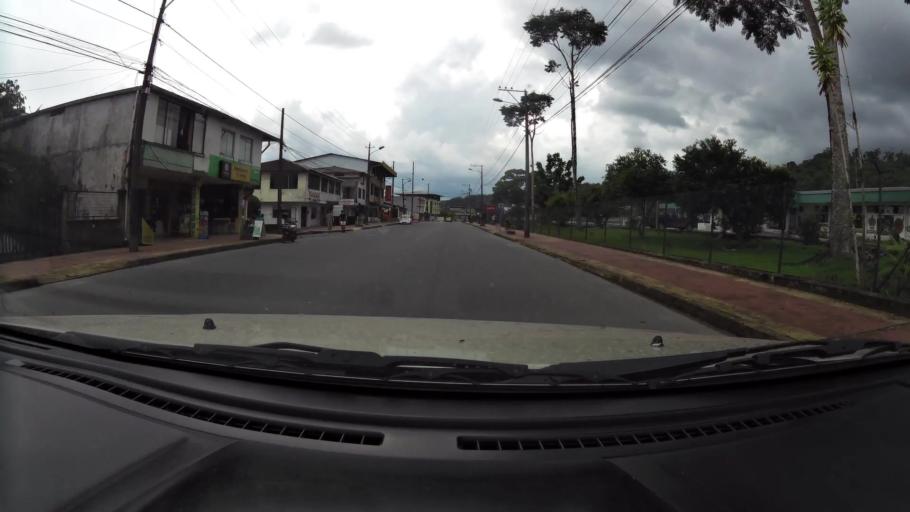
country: EC
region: Pastaza
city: Puyo
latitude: -1.4909
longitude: -78.0136
